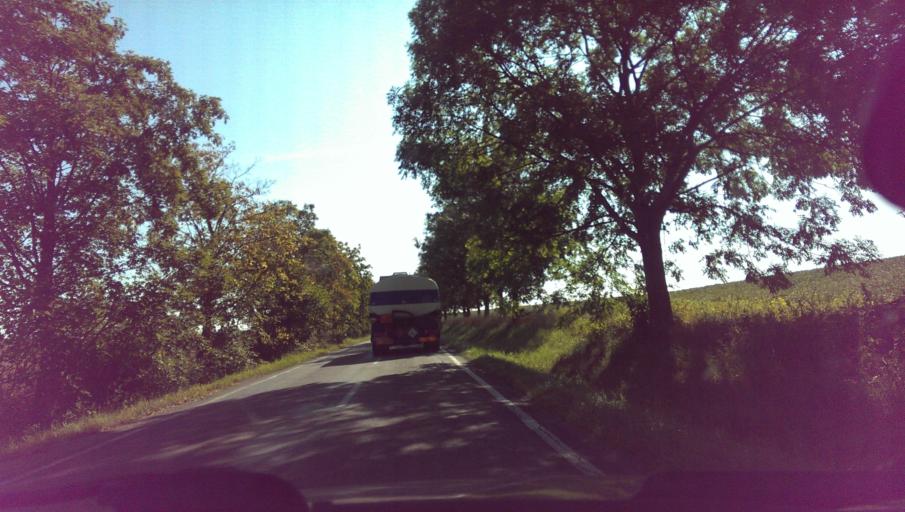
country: CZ
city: Brusperk
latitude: 49.6884
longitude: 18.2088
